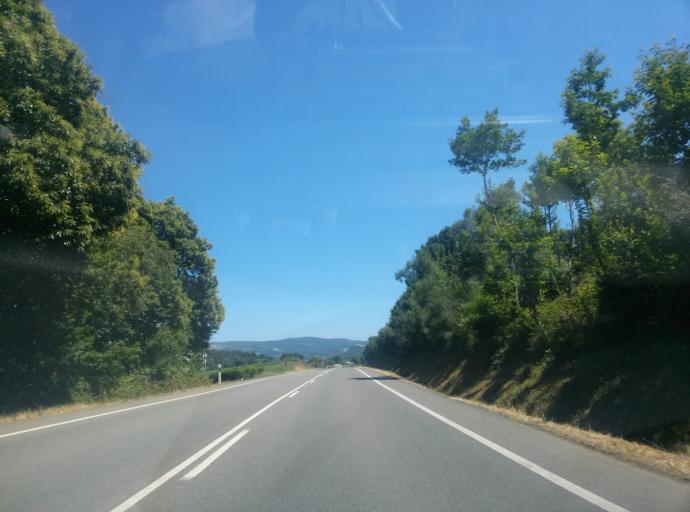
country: ES
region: Galicia
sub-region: Provincia de Lugo
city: Meira
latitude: 43.2307
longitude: -7.3369
